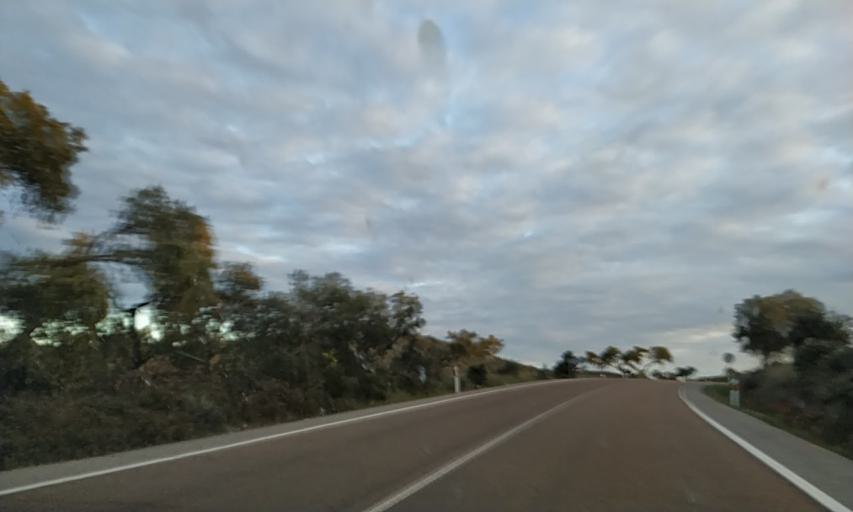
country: ES
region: Extremadura
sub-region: Provincia de Badajoz
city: Puebla de Obando
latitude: 39.2133
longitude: -6.5830
